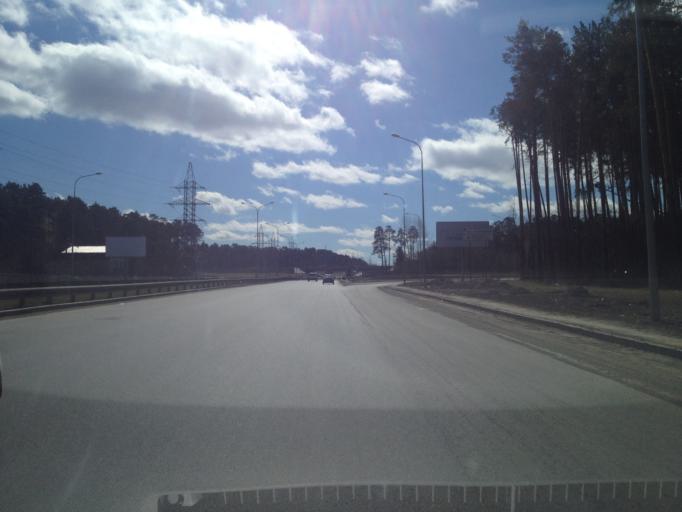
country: RU
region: Sverdlovsk
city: Sovkhoznyy
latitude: 56.7947
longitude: 60.5964
